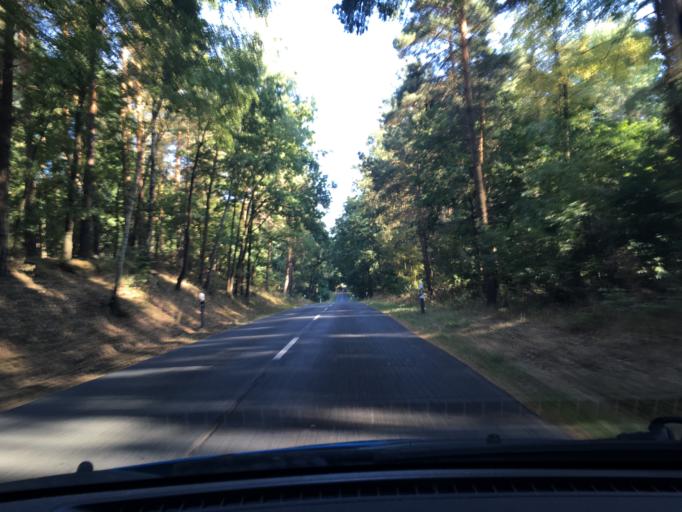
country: DE
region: Lower Saxony
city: Dahlenburg
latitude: 53.2075
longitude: 10.7084
